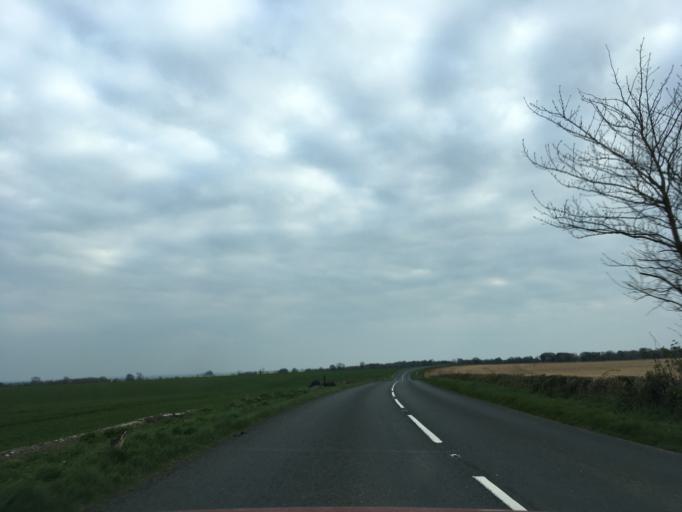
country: GB
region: England
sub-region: Gloucestershire
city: Nailsworth
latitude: 51.6494
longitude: -2.2374
